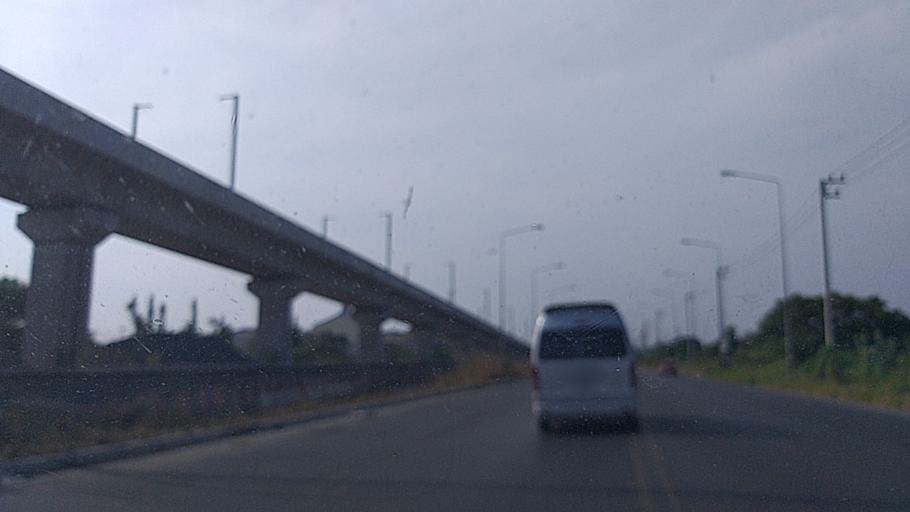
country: TH
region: Phra Nakhon Si Ayutthaya
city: Ban Bang Kadi Pathum Thani
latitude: 13.9839
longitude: 100.6027
